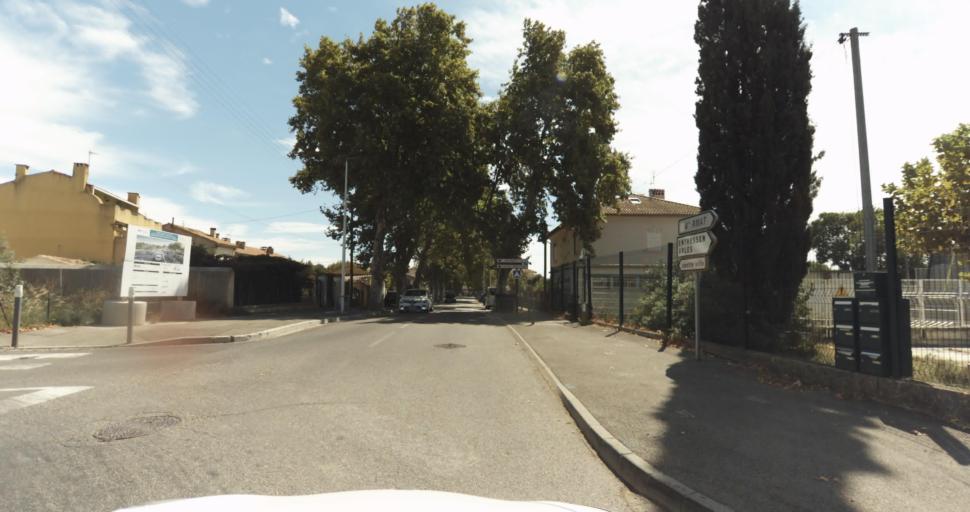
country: FR
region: Provence-Alpes-Cote d'Azur
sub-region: Departement des Bouches-du-Rhone
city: Miramas
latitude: 43.5831
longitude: 4.9946
